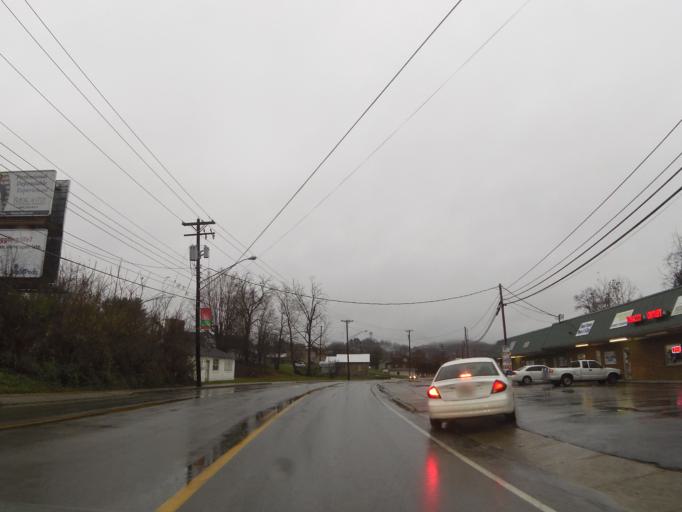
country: US
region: Kentucky
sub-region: Rockcastle County
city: Mount Vernon
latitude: 37.3607
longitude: -84.3368
